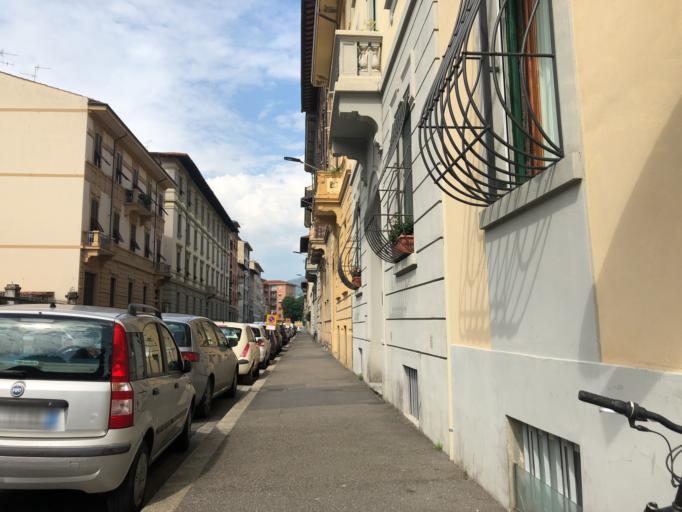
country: IT
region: Tuscany
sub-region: Province of Florence
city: Florence
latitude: 43.7728
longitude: 11.2754
